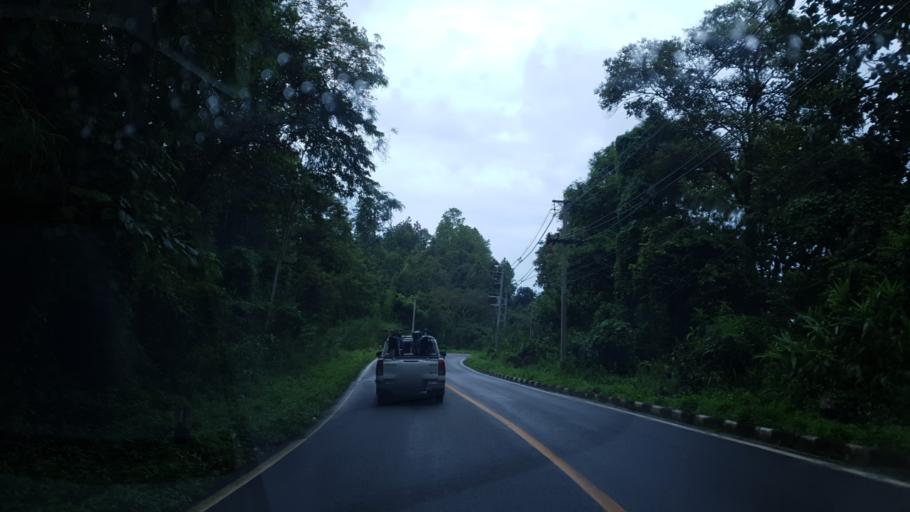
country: TH
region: Mae Hong Son
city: Ban Huai I Huak
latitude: 18.1521
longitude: 98.0270
